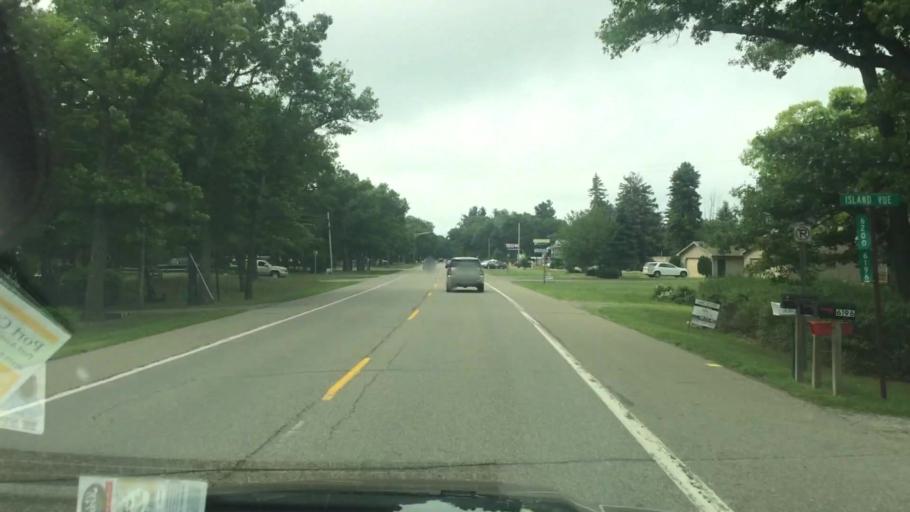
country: US
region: Michigan
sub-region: Huron County
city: Pigeon
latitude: 43.9630
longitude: -83.2629
